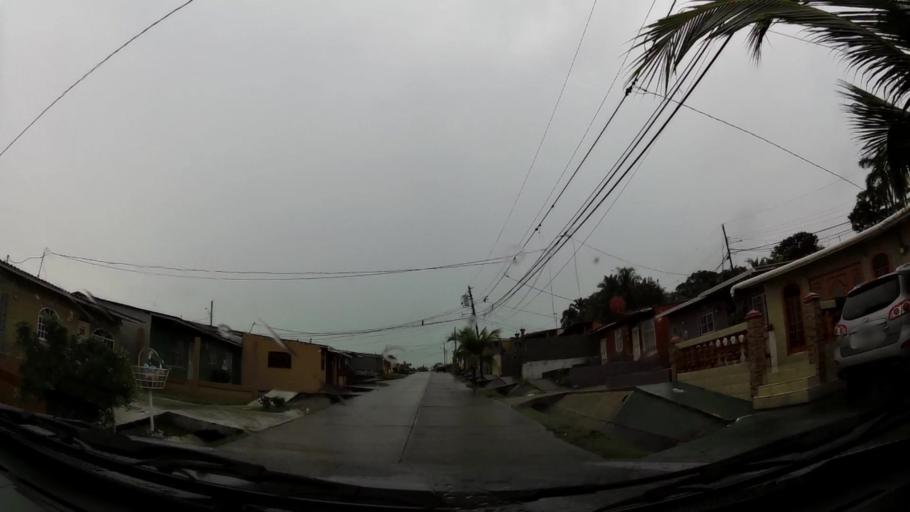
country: PA
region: Colon
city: Puerto Pilon
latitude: 9.3545
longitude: -79.7924
